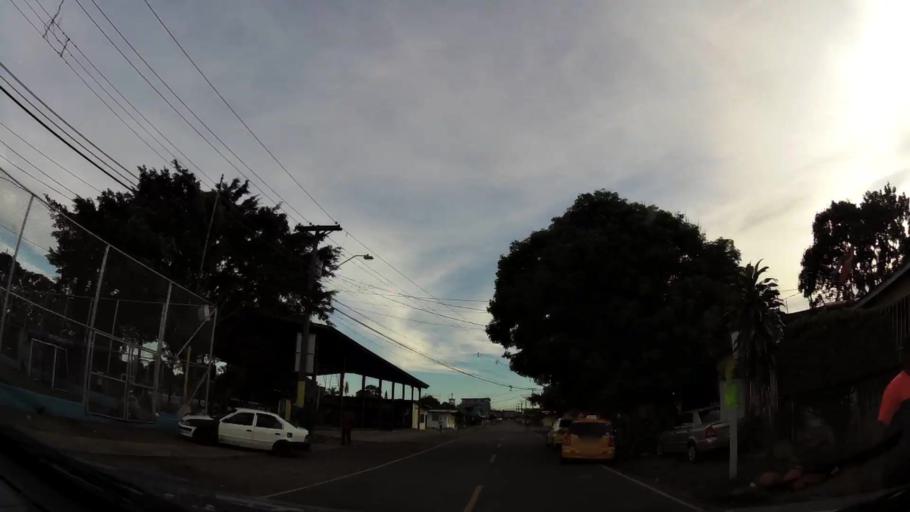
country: PA
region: Panama
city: La Chorrera
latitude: 8.8872
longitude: -79.7814
